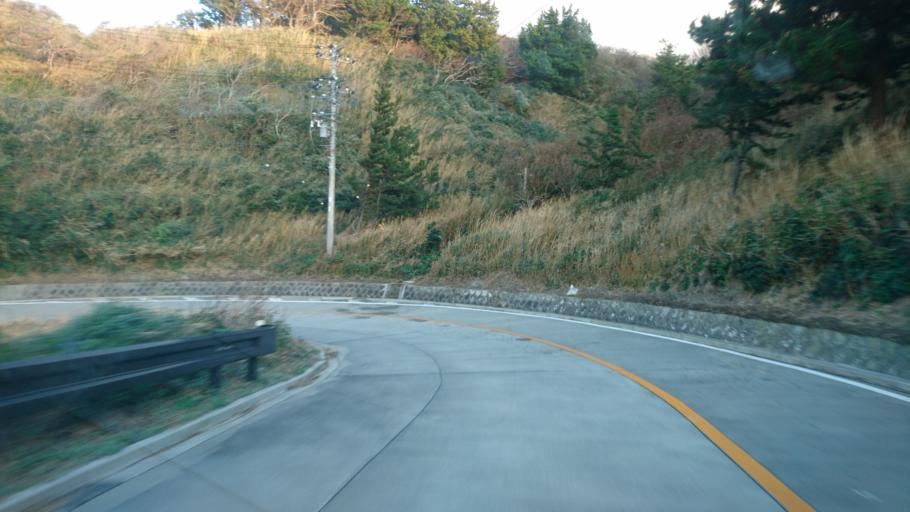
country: JP
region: Shizuoka
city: Shimoda
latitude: 34.3652
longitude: 139.2440
